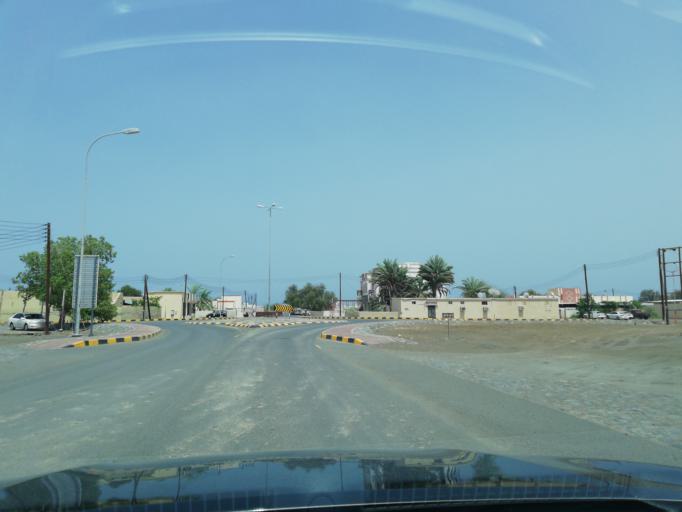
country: OM
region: Al Batinah
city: Shinas
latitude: 24.7392
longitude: 56.4650
